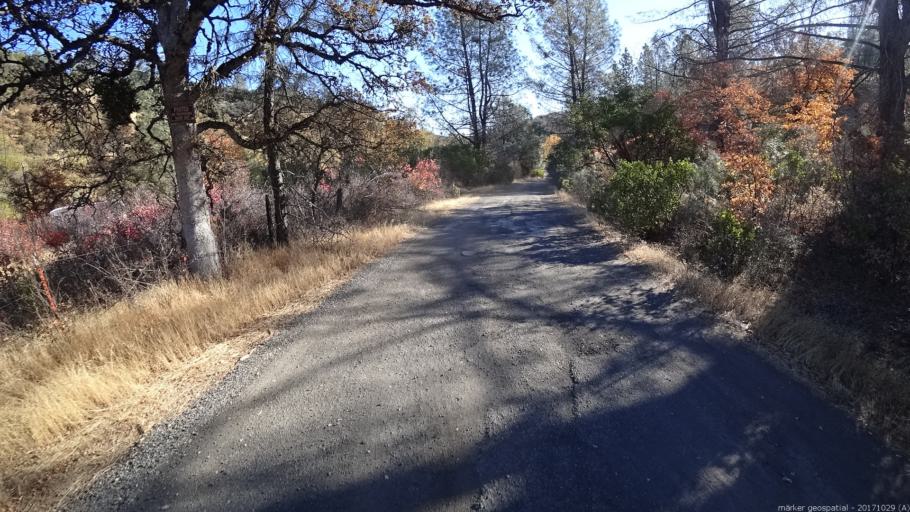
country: US
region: California
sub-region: Trinity County
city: Hayfork
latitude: 40.3586
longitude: -122.9004
